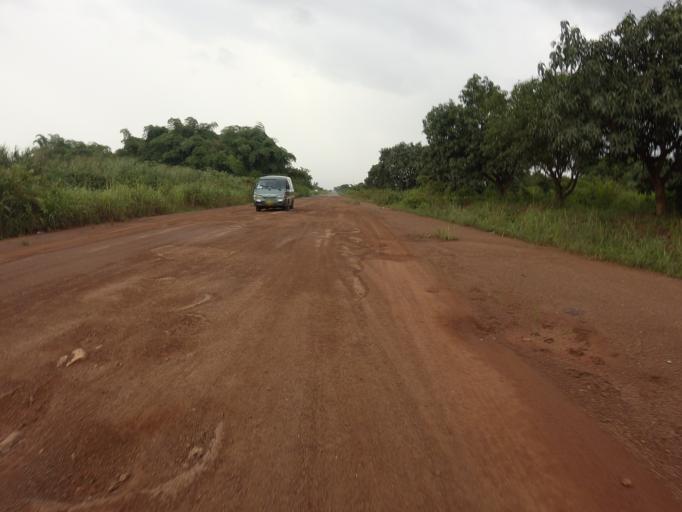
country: GH
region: Volta
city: Kpandu
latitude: 7.0205
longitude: 0.4281
